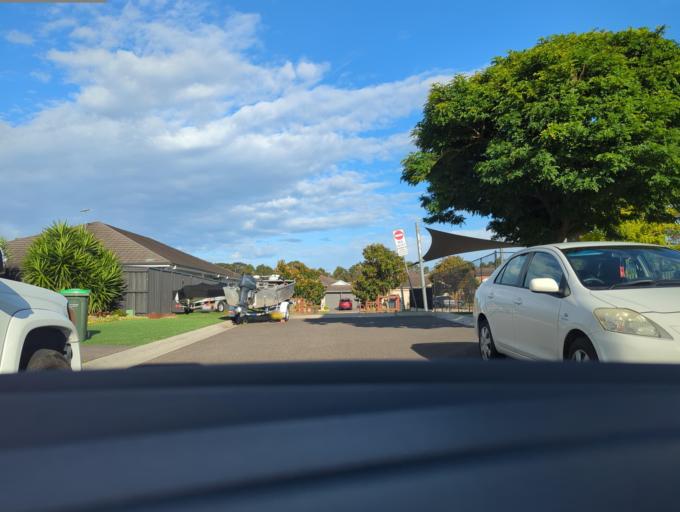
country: AU
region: New South Wales
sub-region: Sutherland Shire
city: Menai
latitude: -34.0270
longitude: 151.0036
